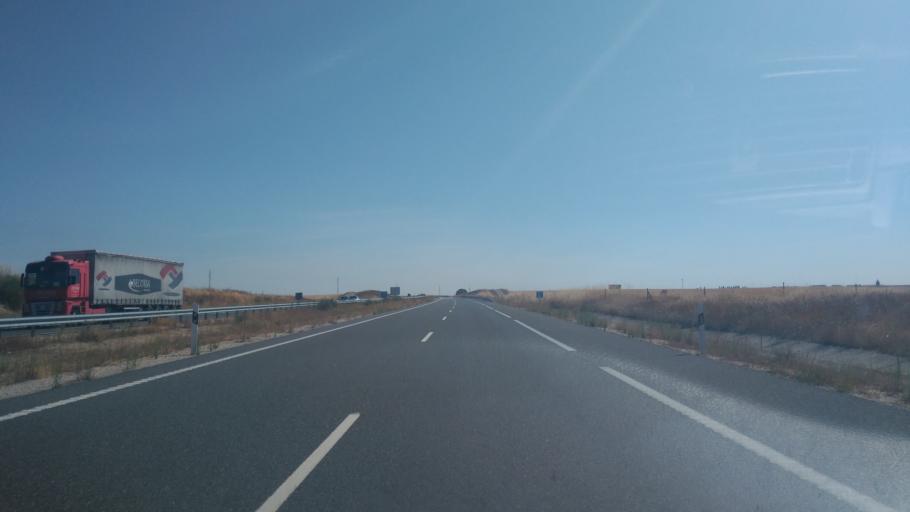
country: ES
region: Castille and Leon
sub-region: Provincia de Salamanca
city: Alconada
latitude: 40.9304
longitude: -5.3685
